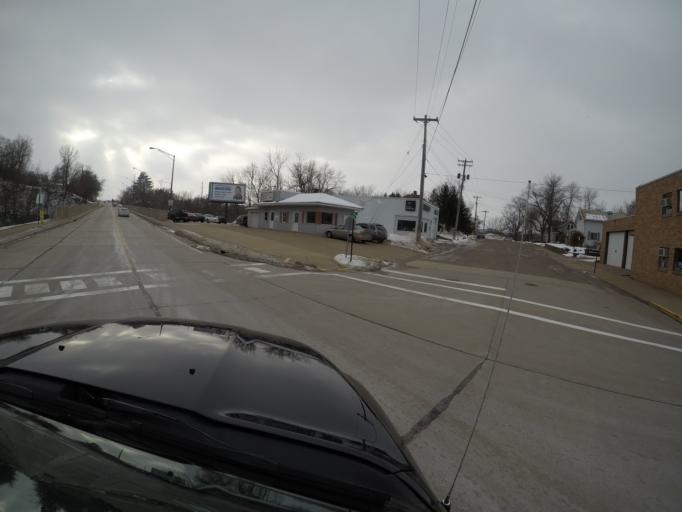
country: US
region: Wisconsin
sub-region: Trempealeau County
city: Galesville
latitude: 44.0814
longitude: -91.3490
